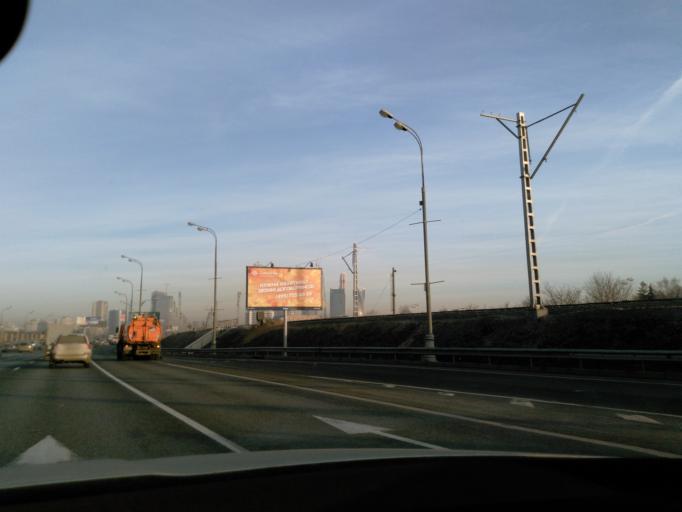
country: RU
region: Moscow
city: Luzhniki
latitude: 55.7238
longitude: 37.5519
